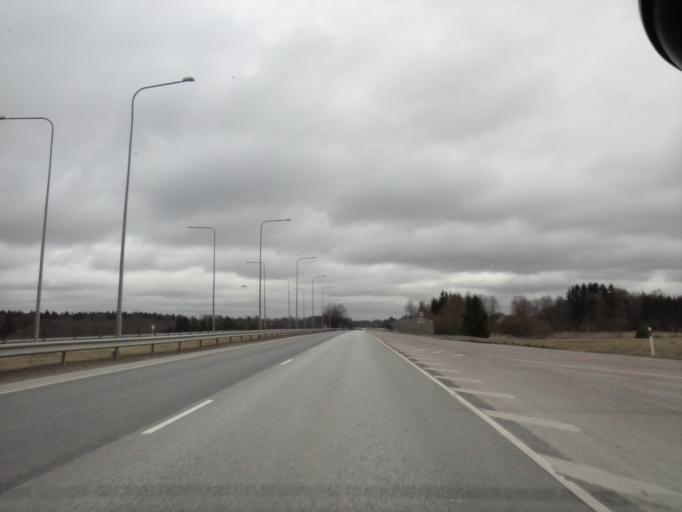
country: EE
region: Harju
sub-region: Rae vald
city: Vaida
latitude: 59.3117
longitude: 24.9360
